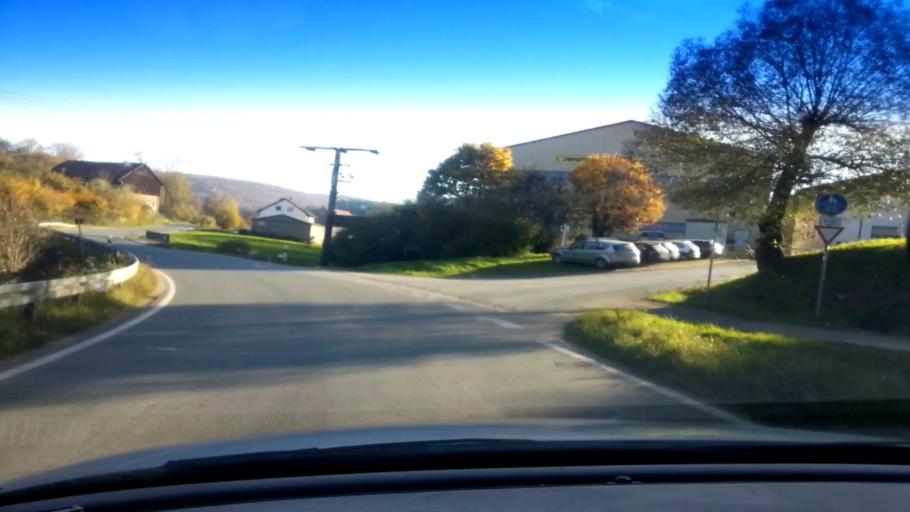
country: DE
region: Bavaria
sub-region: Upper Franconia
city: Poxdorf
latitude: 49.8872
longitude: 11.1278
